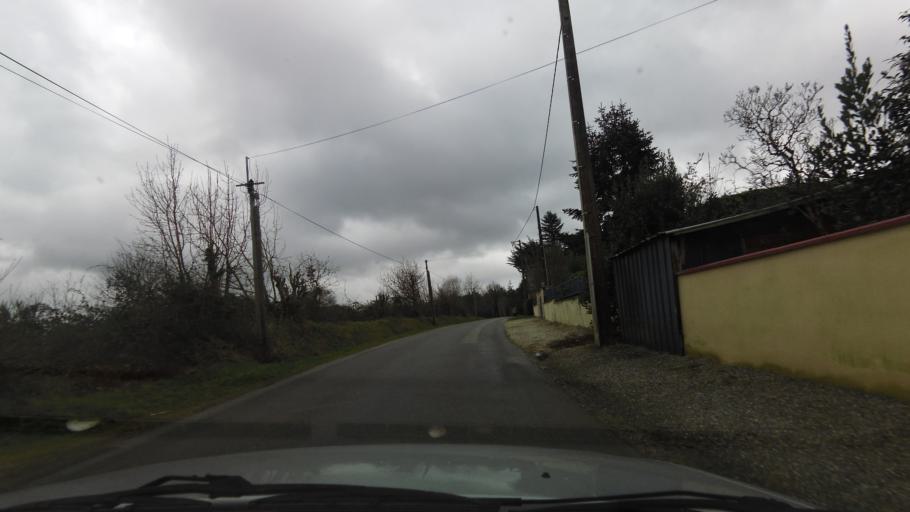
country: FR
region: Brittany
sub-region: Departement du Morbihan
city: Elven
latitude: 47.7945
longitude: -2.5809
